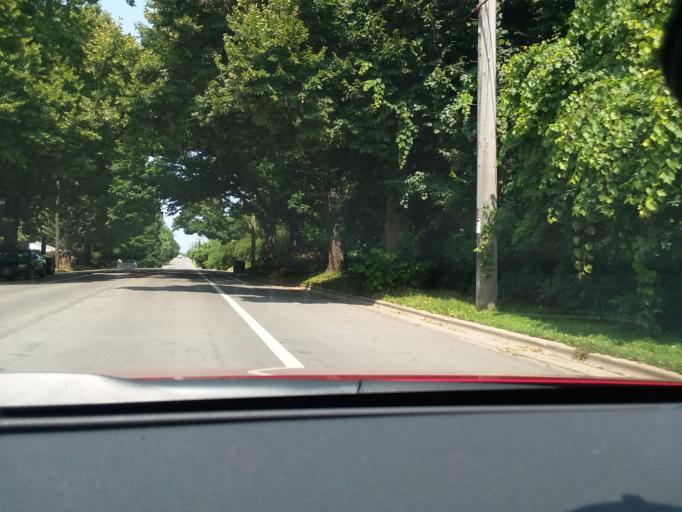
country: US
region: Wisconsin
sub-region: Dane County
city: Monona
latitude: 43.1148
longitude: -89.3162
